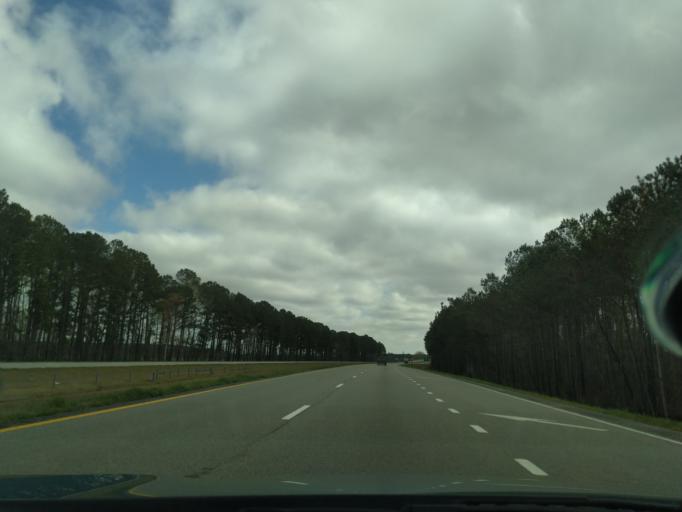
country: US
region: North Carolina
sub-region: Chowan County
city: Edenton
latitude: 36.0854
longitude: -76.5932
